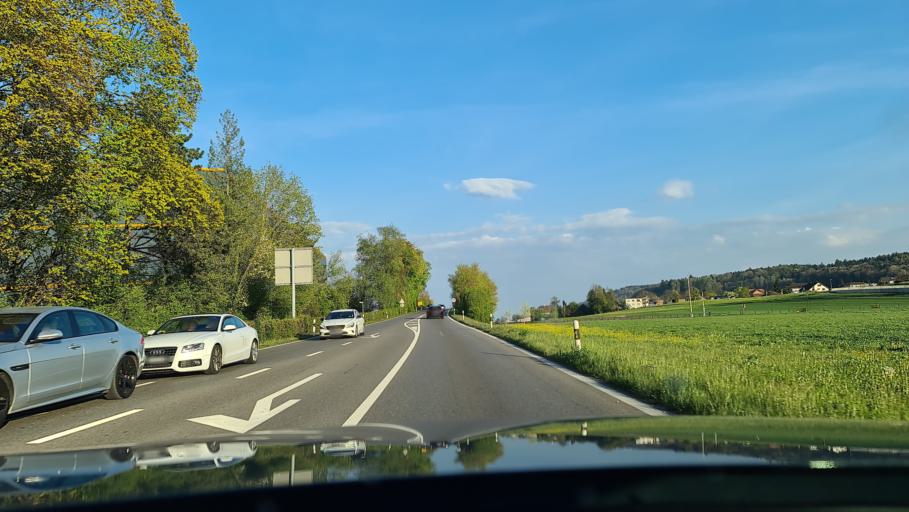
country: CH
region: Aargau
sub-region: Bezirk Bremgarten
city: Villmergen
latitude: 47.3520
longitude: 8.2536
